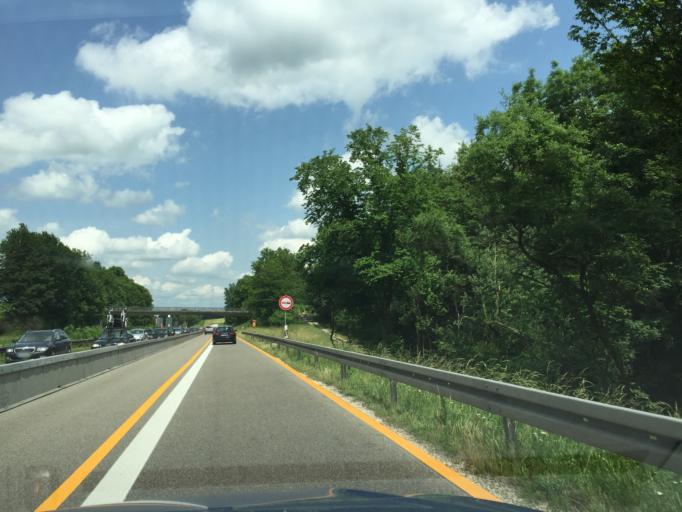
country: DE
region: Bavaria
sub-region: Swabia
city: Holzheim
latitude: 48.3724
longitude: 10.0843
